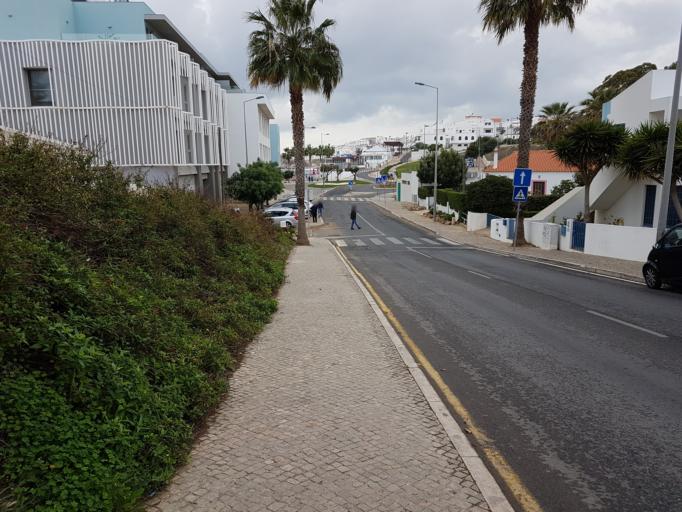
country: PT
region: Faro
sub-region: Albufeira
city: Albufeira
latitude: 37.0863
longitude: -8.2428
